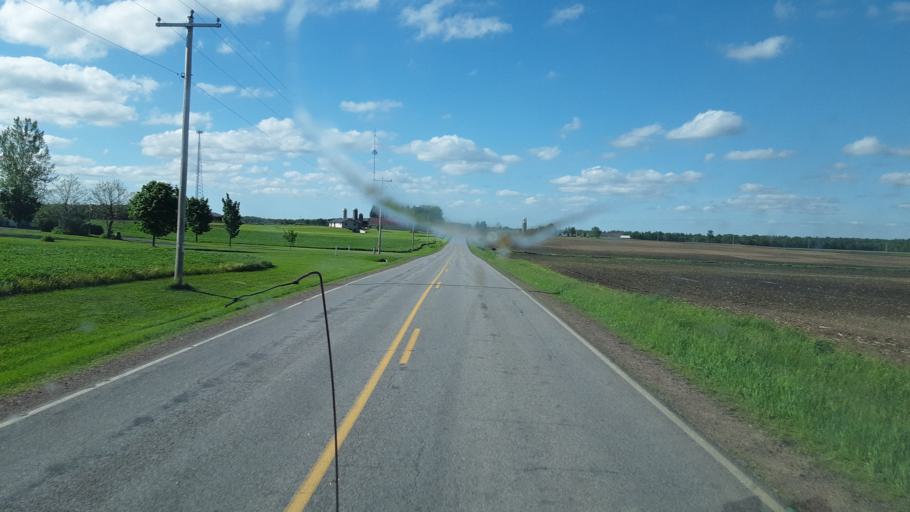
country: US
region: Wisconsin
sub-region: Wood County
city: Marshfield
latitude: 44.4325
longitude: -90.1601
